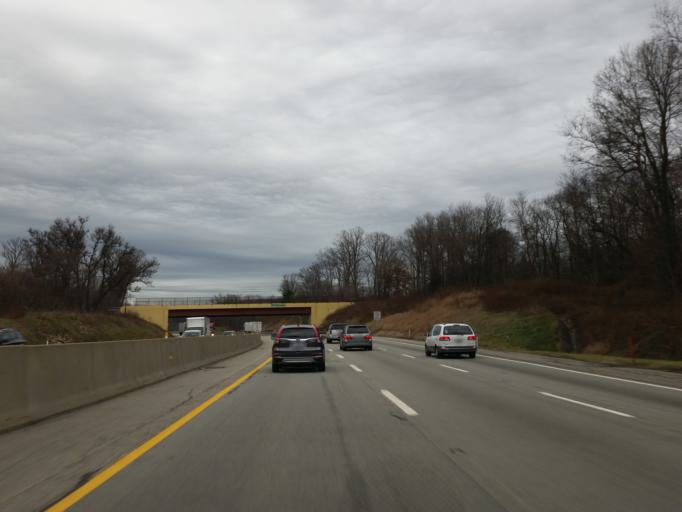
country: US
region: Pennsylvania
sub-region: Fayette County
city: Bear Rocks
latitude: 40.1464
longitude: -79.4247
